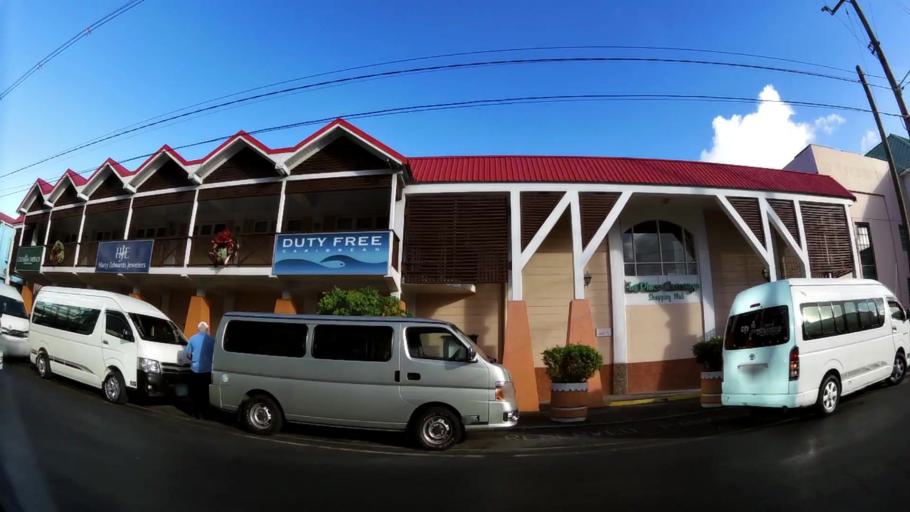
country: LC
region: Castries Quarter
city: Bisee
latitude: 14.0112
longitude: -60.9911
